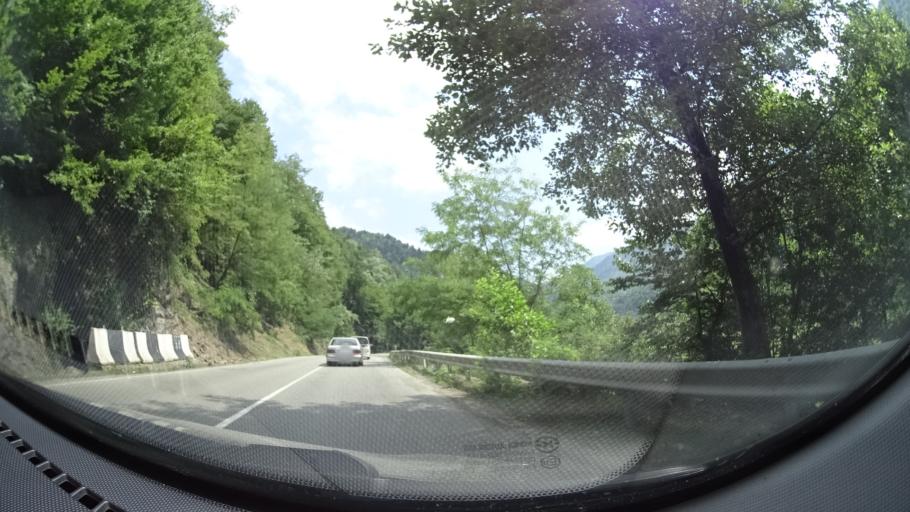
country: GE
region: Ajaria
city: Keda
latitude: 41.5690
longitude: 41.8448
